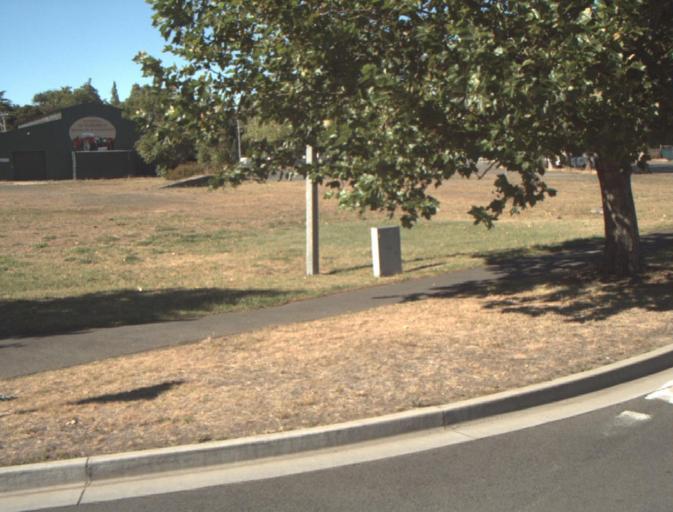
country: AU
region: Tasmania
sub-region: Launceston
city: East Launceston
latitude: -41.4303
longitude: 147.1427
